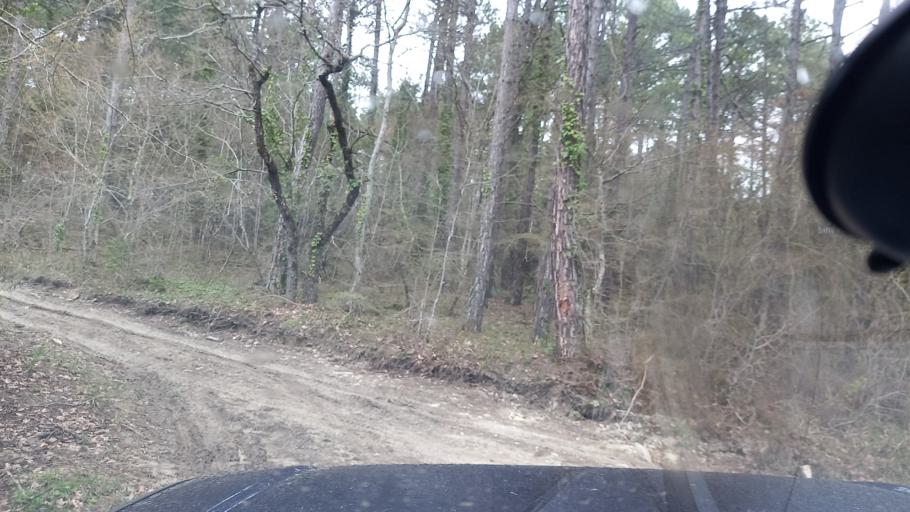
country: RU
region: Krasnodarskiy
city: Arkhipo-Osipovka
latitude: 44.3750
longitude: 38.4739
